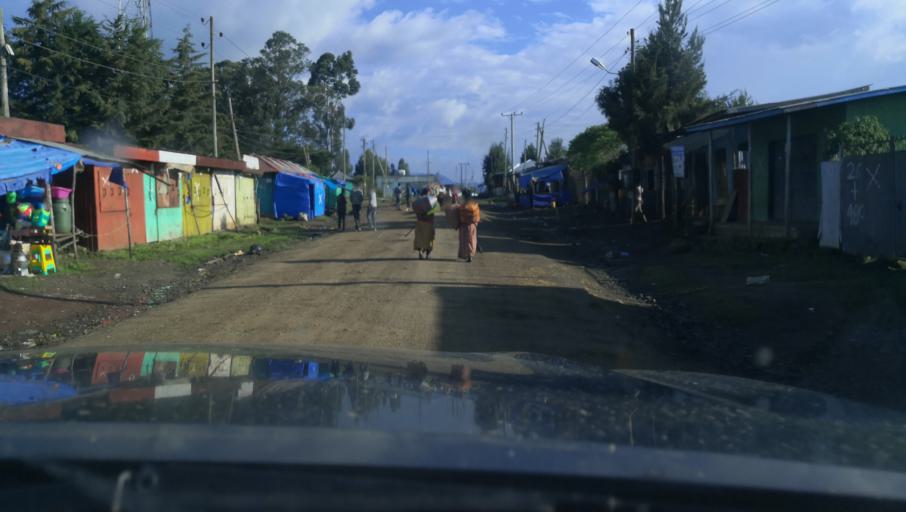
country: ET
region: Oromiya
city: Tulu Bolo
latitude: 8.4639
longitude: 38.2524
